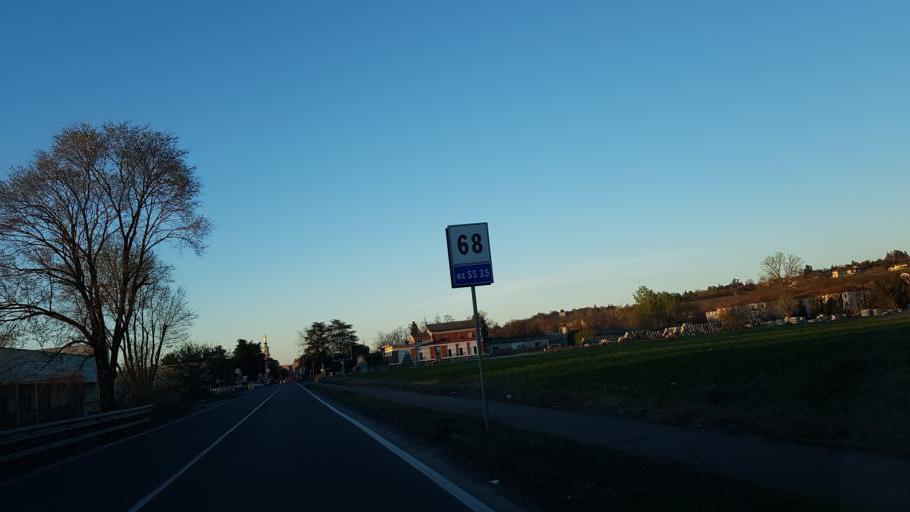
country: IT
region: Piedmont
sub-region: Provincia di Alessandria
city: Tortona
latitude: 44.8782
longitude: 8.8579
